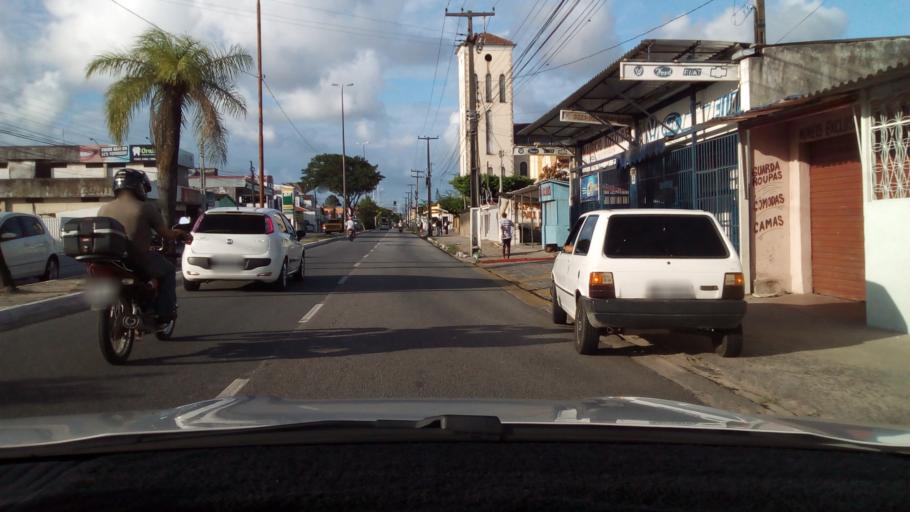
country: BR
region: Paraiba
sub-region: Joao Pessoa
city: Joao Pessoa
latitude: -7.1436
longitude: -34.8909
